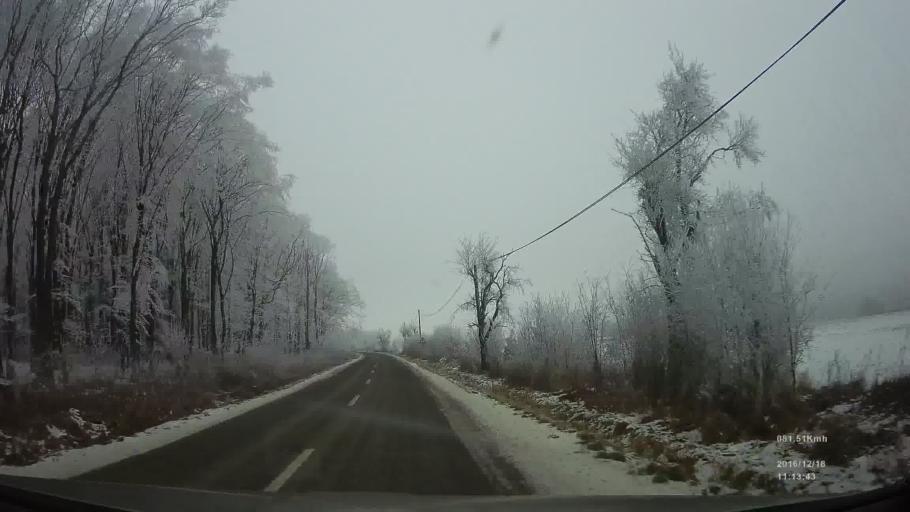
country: SK
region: Presovsky
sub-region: Okres Presov
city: Presov
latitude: 48.8854
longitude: 21.3139
